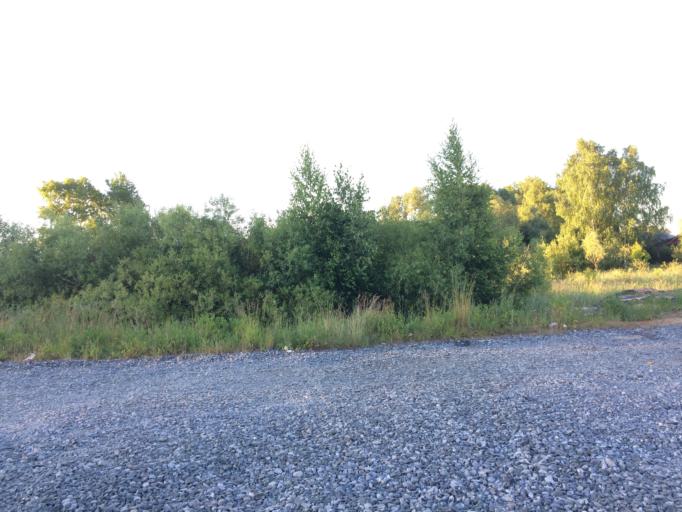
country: RU
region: Mariy-El
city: Yoshkar-Ola
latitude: 56.6557
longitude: 47.8985
